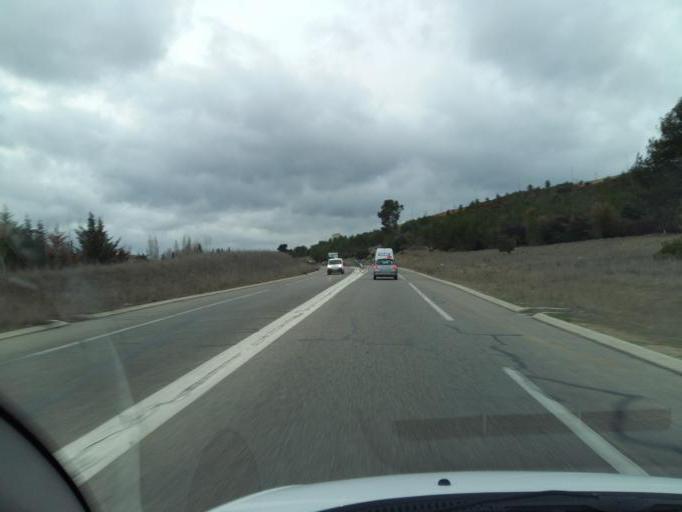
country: FR
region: Provence-Alpes-Cote d'Azur
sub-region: Departement des Bouches-du-Rhone
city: Cabries
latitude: 43.4830
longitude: 5.3537
